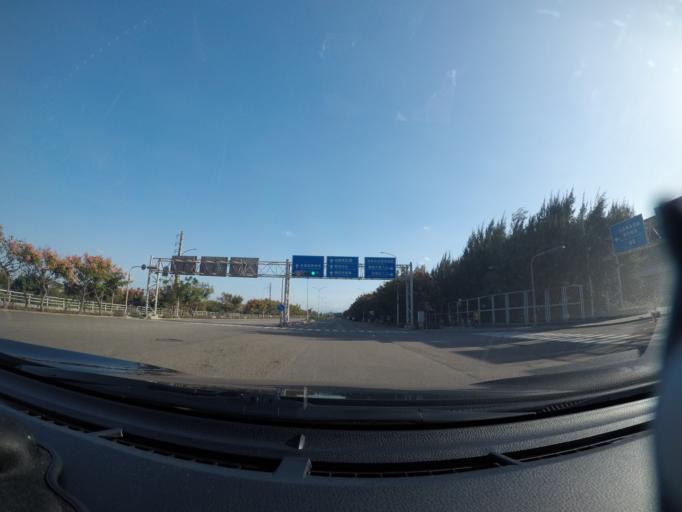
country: TW
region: Taiwan
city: Taoyuan City
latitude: 25.0996
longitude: 121.2549
